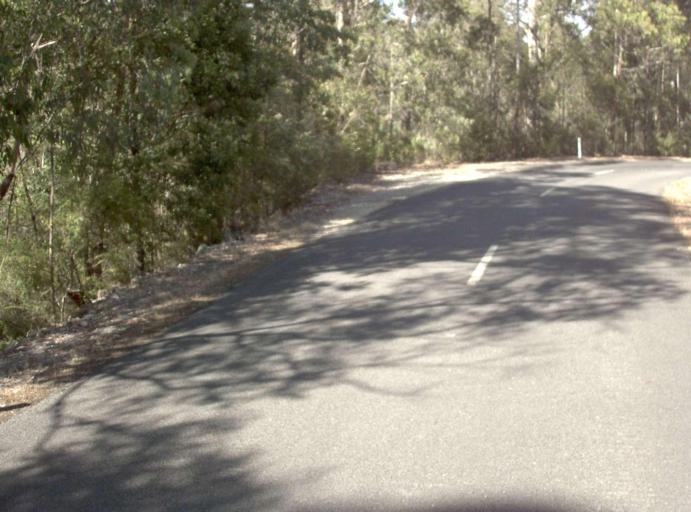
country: AU
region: Victoria
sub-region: East Gippsland
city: Lakes Entrance
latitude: -37.5023
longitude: 148.5482
